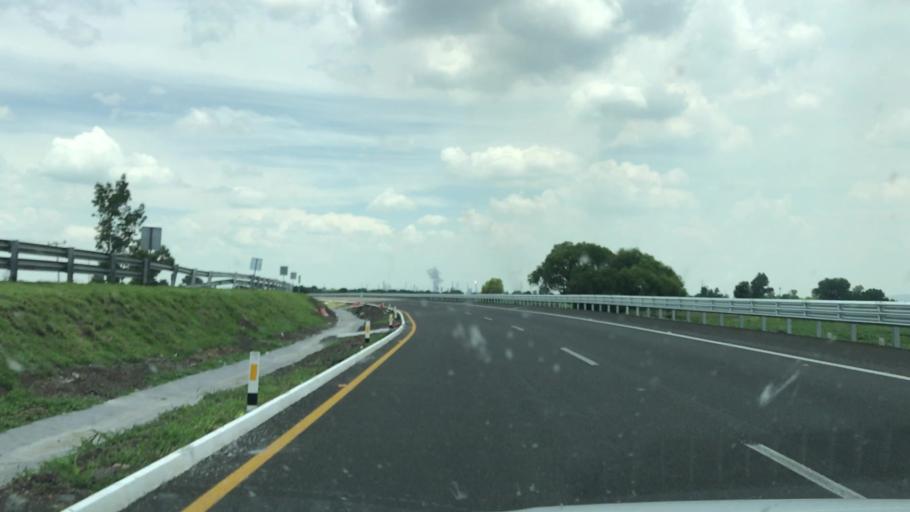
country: MX
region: Guanajuato
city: Salamanca
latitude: 20.6045
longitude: -101.2095
